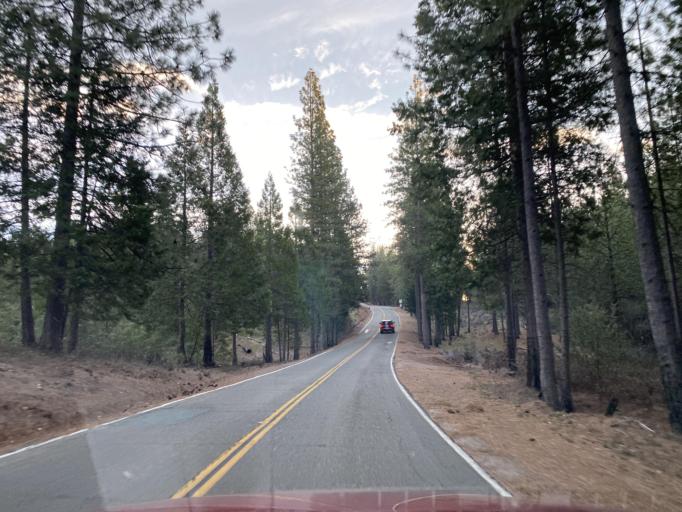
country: US
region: California
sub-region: Amador County
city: Pine Grove
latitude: 38.5013
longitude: -120.6463
